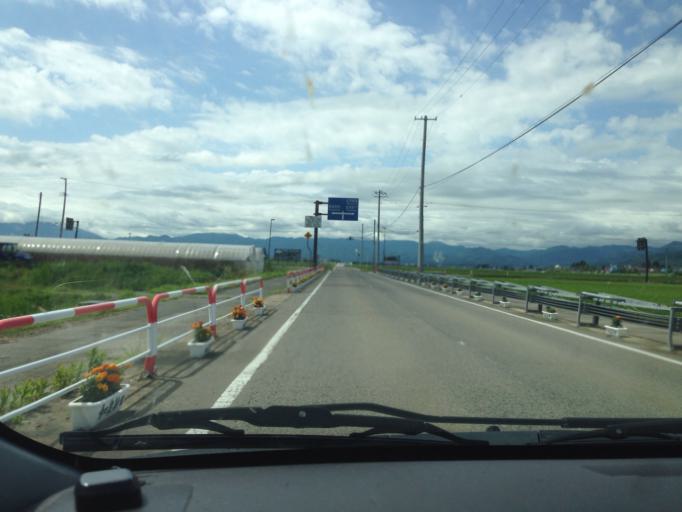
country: JP
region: Fukushima
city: Kitakata
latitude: 37.5274
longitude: 139.8399
